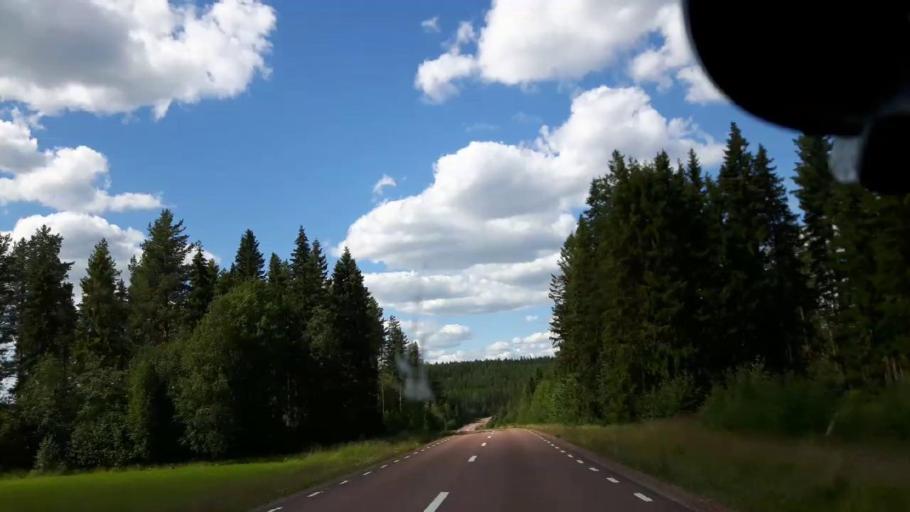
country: SE
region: Jaemtland
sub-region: Ragunda Kommun
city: Hammarstrand
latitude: 63.0203
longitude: 16.5516
